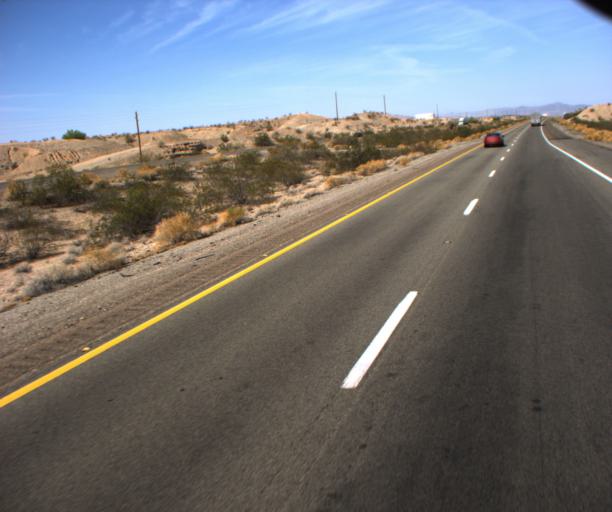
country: US
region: Arizona
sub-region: Mohave County
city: Desert Hills
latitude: 34.7328
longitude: -114.2651
